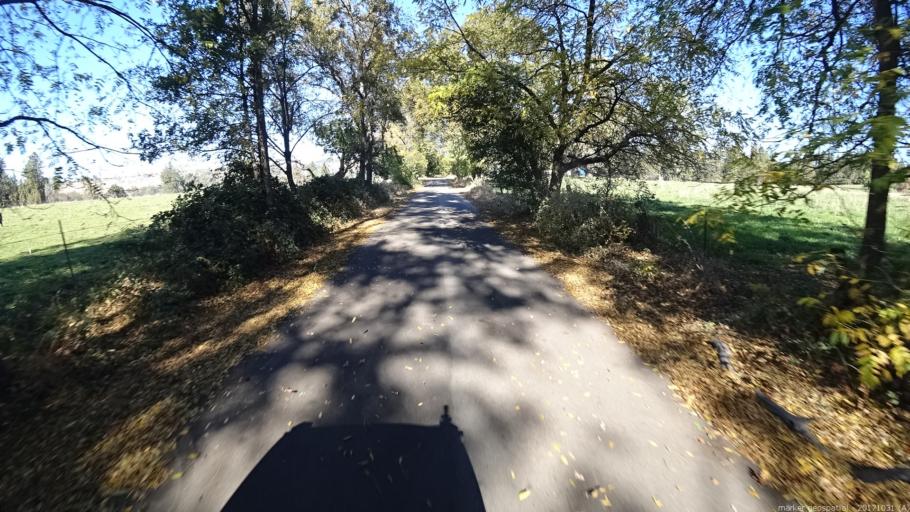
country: US
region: California
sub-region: Shasta County
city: Shingletown
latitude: 40.5282
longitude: -121.9546
